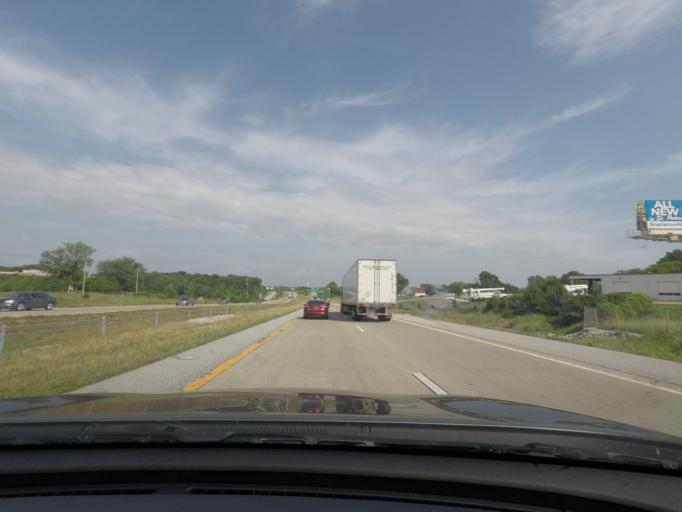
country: US
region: Missouri
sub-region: Saint Charles County
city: Wentzville
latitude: 38.8008
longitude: -90.8267
